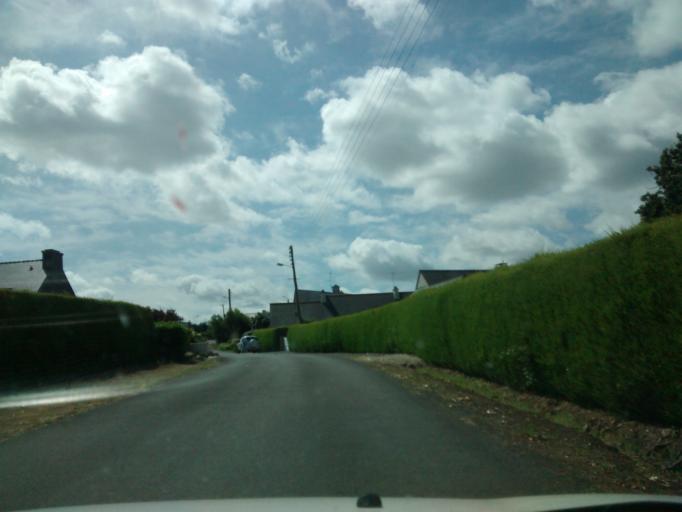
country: FR
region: Brittany
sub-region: Departement des Cotes-d'Armor
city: Penvenan
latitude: 48.8335
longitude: -3.2829
